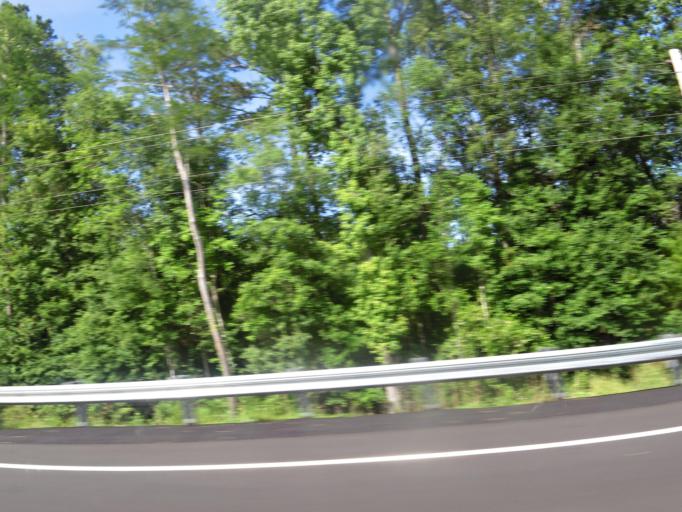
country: US
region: Florida
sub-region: Nassau County
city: Hilliard
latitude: 30.6306
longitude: -81.8953
